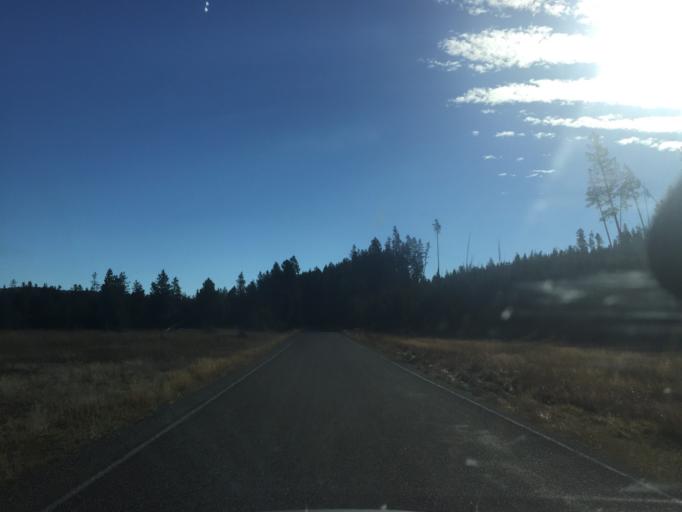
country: US
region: Montana
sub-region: Gallatin County
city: West Yellowstone
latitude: 44.5350
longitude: -110.8148
